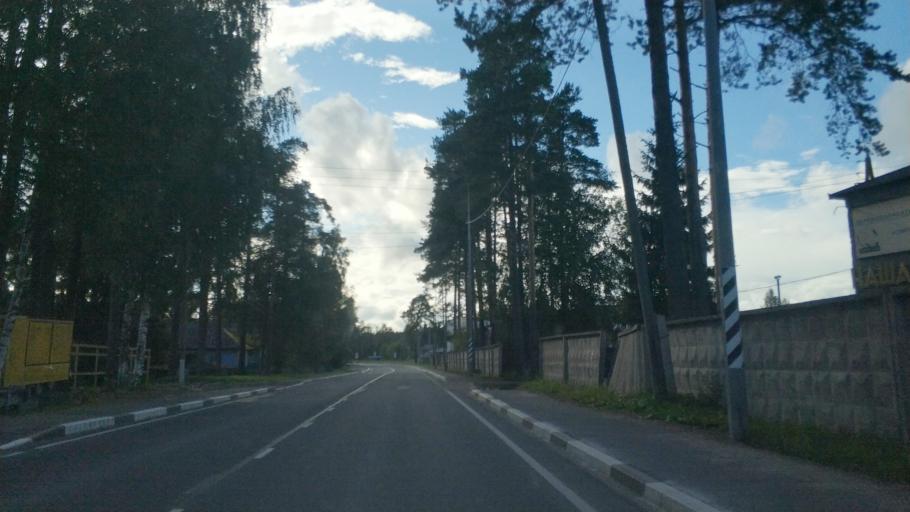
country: RU
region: Republic of Karelia
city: Lakhdenpokh'ya
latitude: 61.5160
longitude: 30.1363
